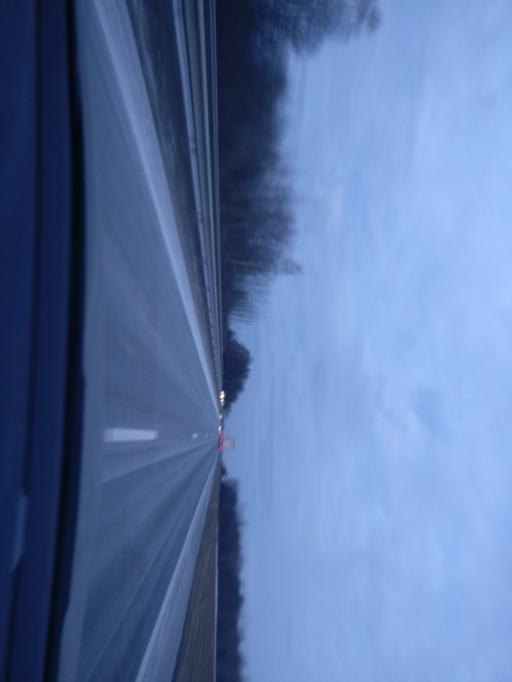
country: LT
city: Kaisiadorys
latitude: 54.8635
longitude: 24.2609
